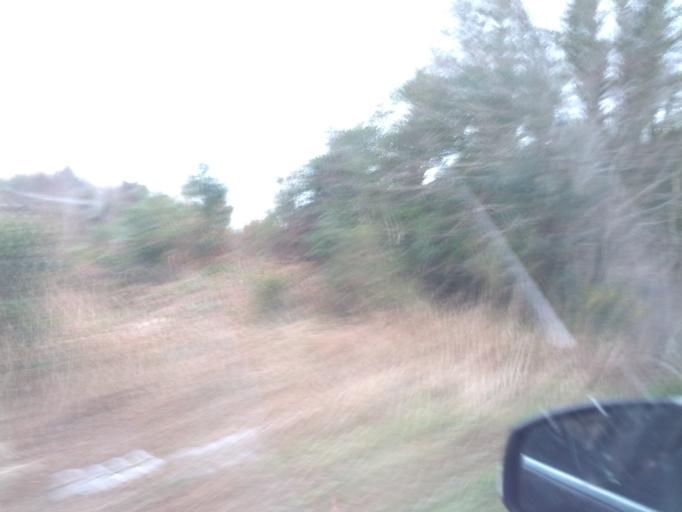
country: IE
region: Connaught
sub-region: County Galway
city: Athenry
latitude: 53.3602
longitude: -8.6444
